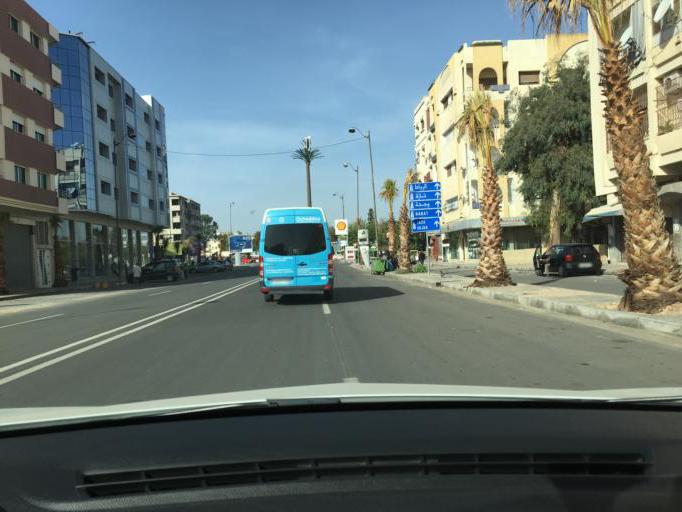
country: MA
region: Fes-Boulemane
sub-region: Fes
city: Fes
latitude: 34.0410
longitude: -5.0129
